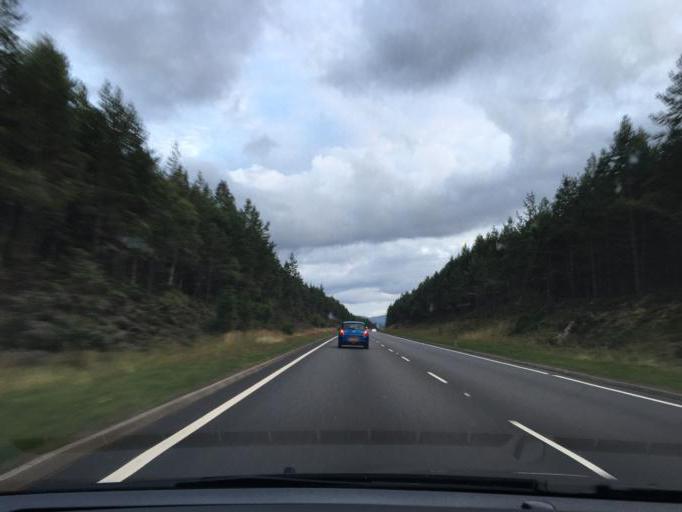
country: GB
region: Scotland
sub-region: Highland
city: Aviemore
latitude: 57.2629
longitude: -3.8119
